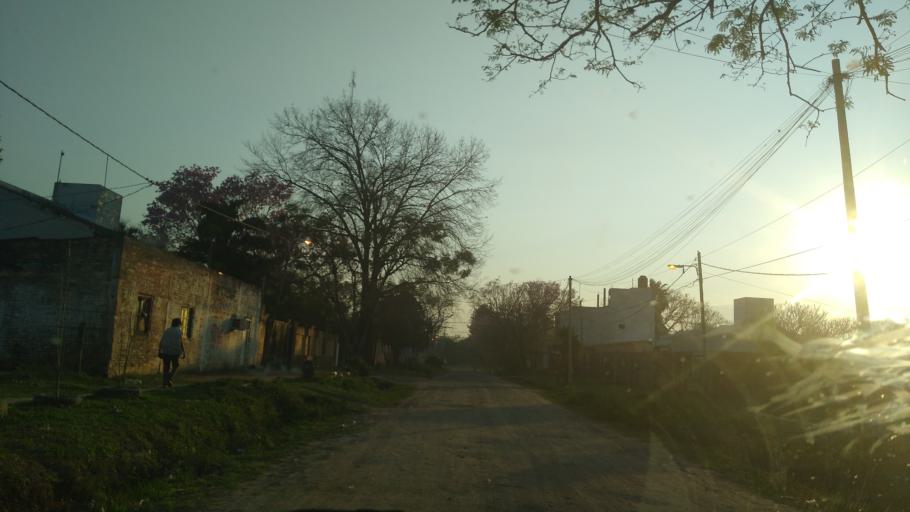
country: AR
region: Chaco
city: Barranqueras
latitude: -27.4701
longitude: -58.9580
